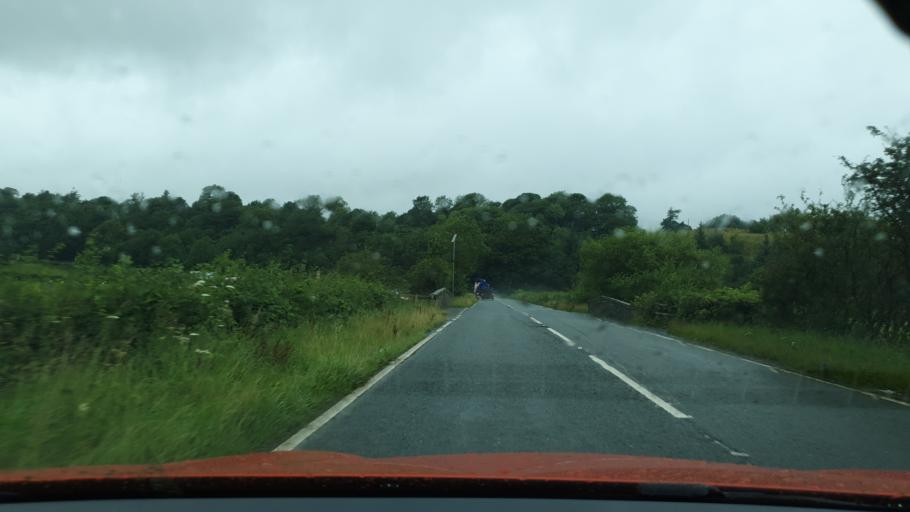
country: GB
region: England
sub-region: Cumbria
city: Askam in Furness
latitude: 54.2687
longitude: -3.1918
